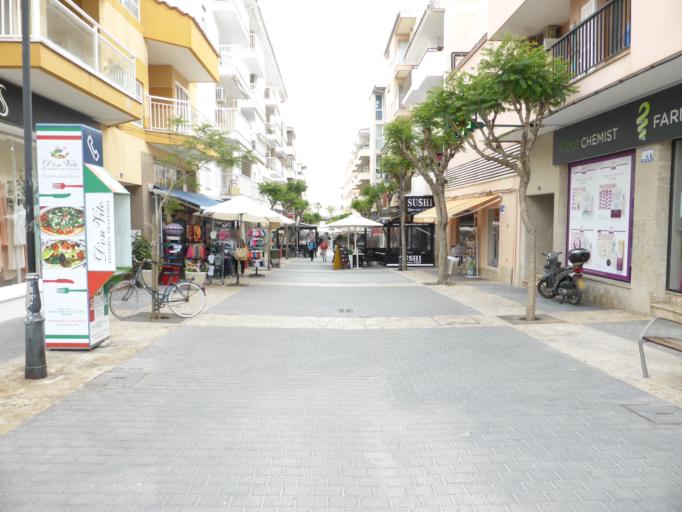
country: ES
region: Balearic Islands
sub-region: Illes Balears
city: Port d'Alcudia
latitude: 39.8429
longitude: 3.1345
